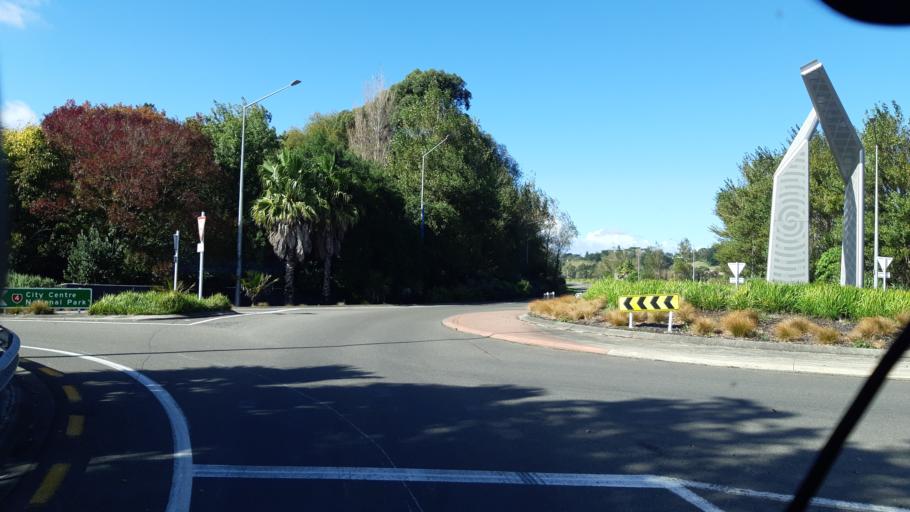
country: NZ
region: Manawatu-Wanganui
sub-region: Wanganui District
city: Wanganui
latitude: -39.9482
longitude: 175.0505
